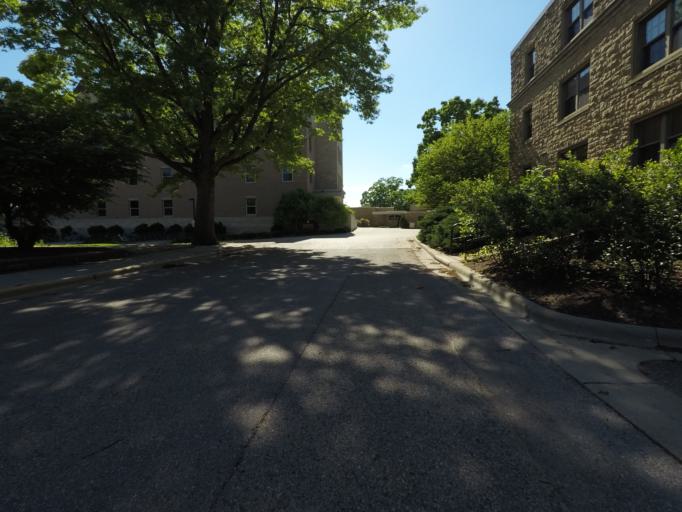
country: US
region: Wisconsin
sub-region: Dane County
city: Madison
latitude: 43.0779
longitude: -89.4134
